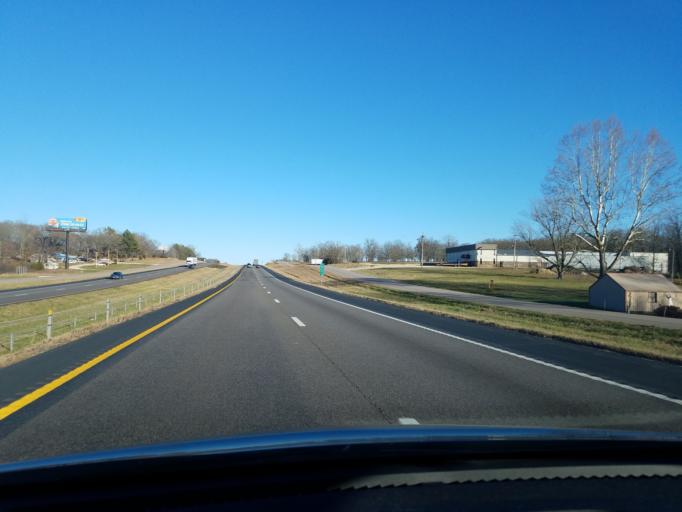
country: US
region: Missouri
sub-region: Phelps County
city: Saint James
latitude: 37.9841
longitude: -91.6857
